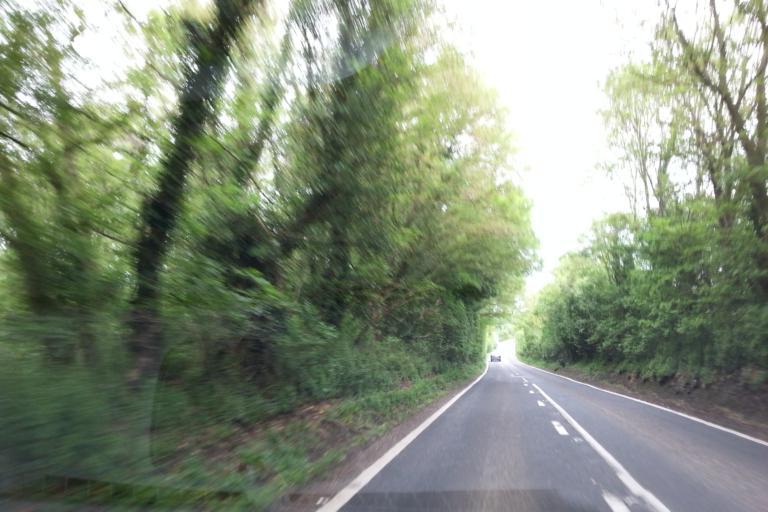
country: GB
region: England
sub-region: Cambridgeshire
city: Ramsey
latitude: 52.4223
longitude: -0.1061
